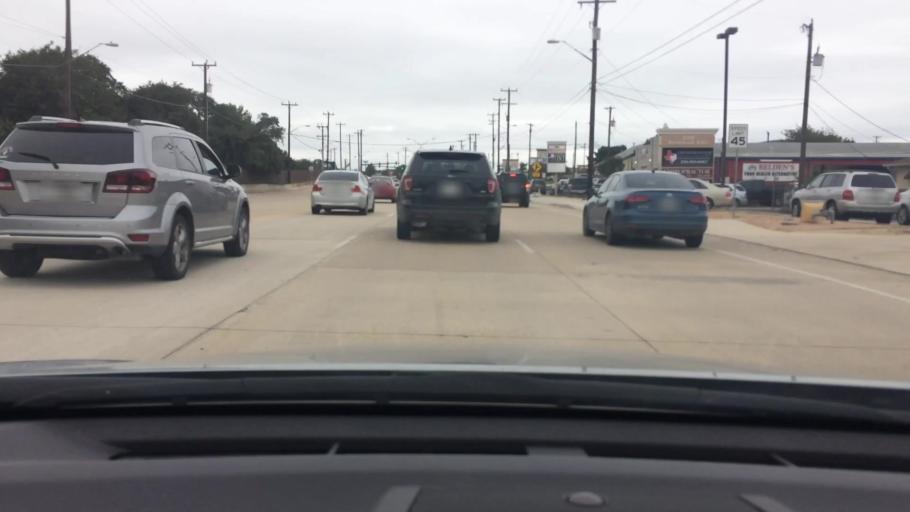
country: US
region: Texas
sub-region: Bexar County
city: Hollywood Park
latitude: 29.6443
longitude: -98.4249
